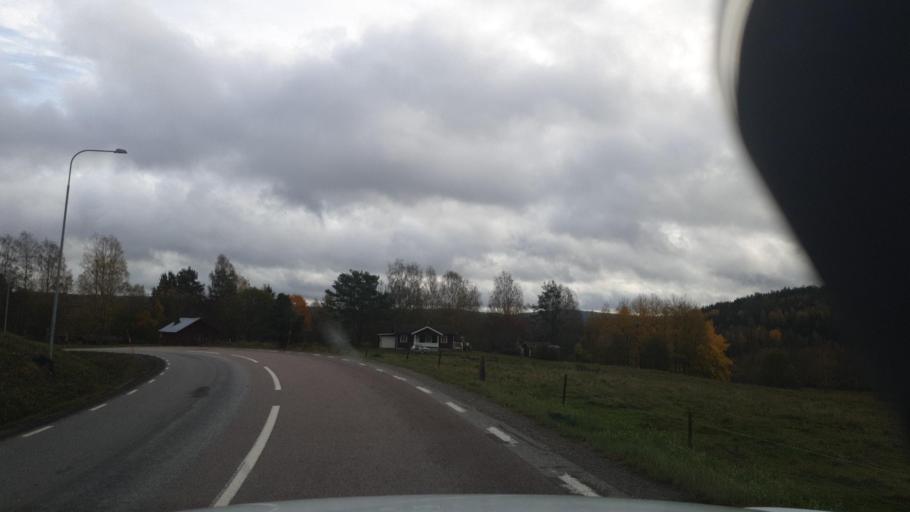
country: SE
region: Vaermland
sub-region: Sunne Kommun
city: Sunne
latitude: 59.6641
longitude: 13.0048
